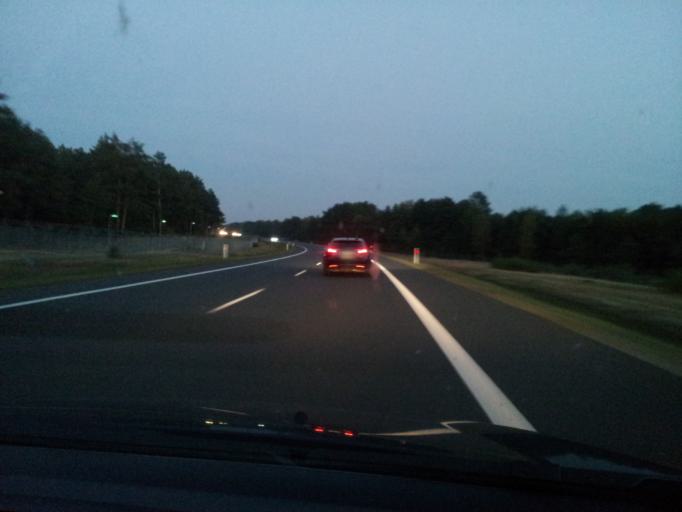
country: PL
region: Kujawsko-Pomorskie
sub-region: Torun
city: Torun
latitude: 52.9765
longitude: 18.6206
